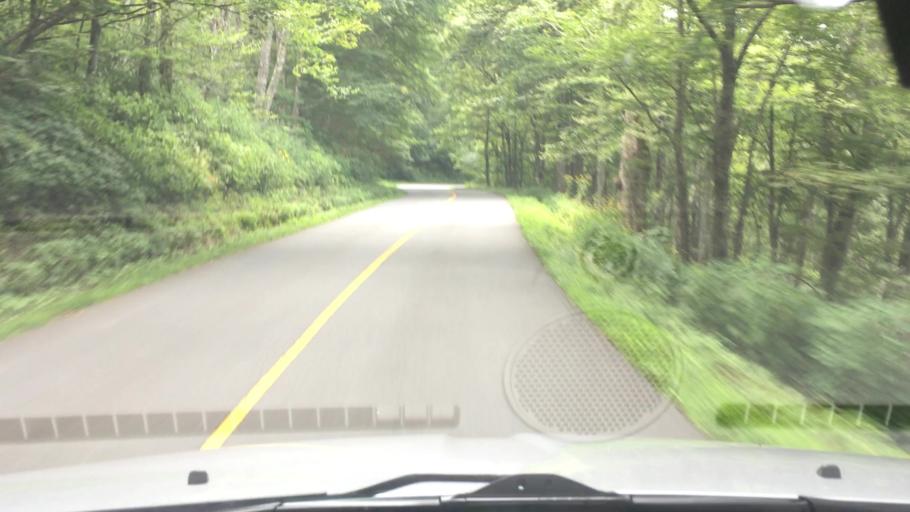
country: US
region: North Carolina
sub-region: Buncombe County
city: Swannanoa
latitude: 35.7016
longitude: -82.3917
